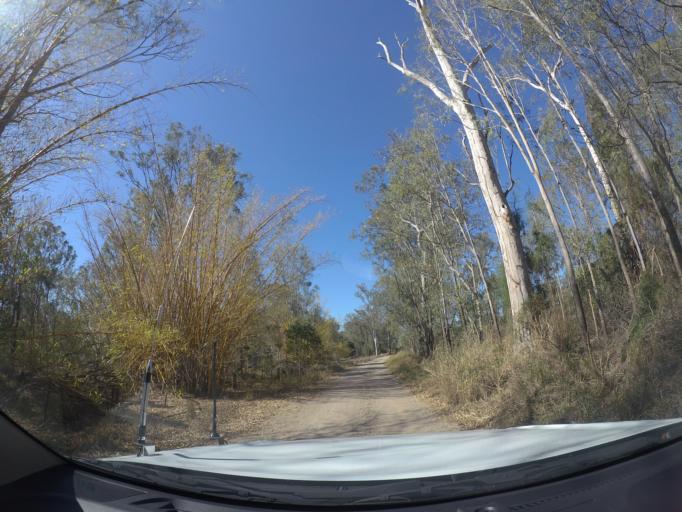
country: AU
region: Queensland
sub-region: Logan
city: North Maclean
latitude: -27.7713
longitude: 153.0151
